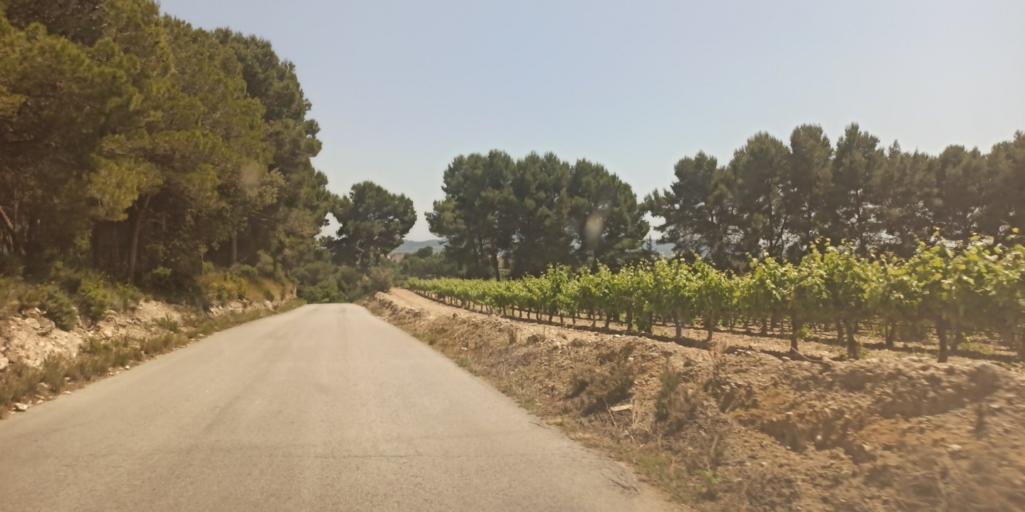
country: ES
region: Catalonia
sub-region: Provincia de Barcelona
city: Vilobi del Penedes
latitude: 41.3768
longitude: 1.6347
